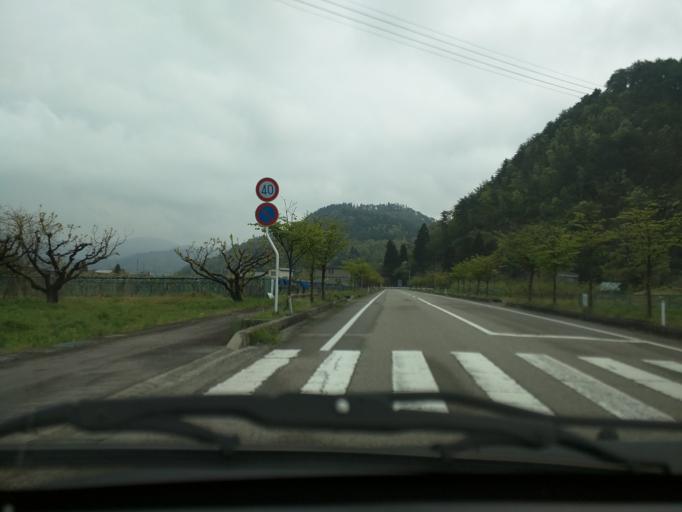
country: JP
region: Fukushima
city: Kitakata
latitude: 37.4533
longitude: 139.8971
